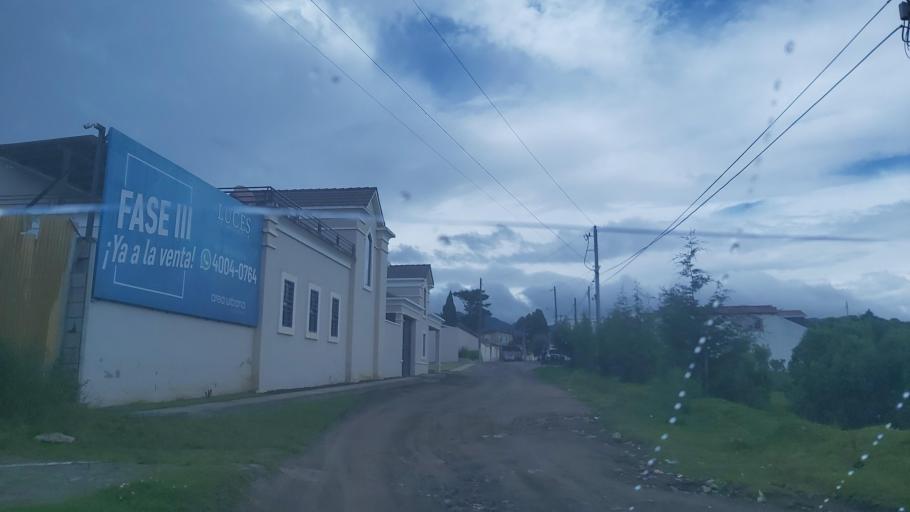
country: GT
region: Quetzaltenango
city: Quetzaltenango
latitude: 14.8536
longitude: -91.5393
